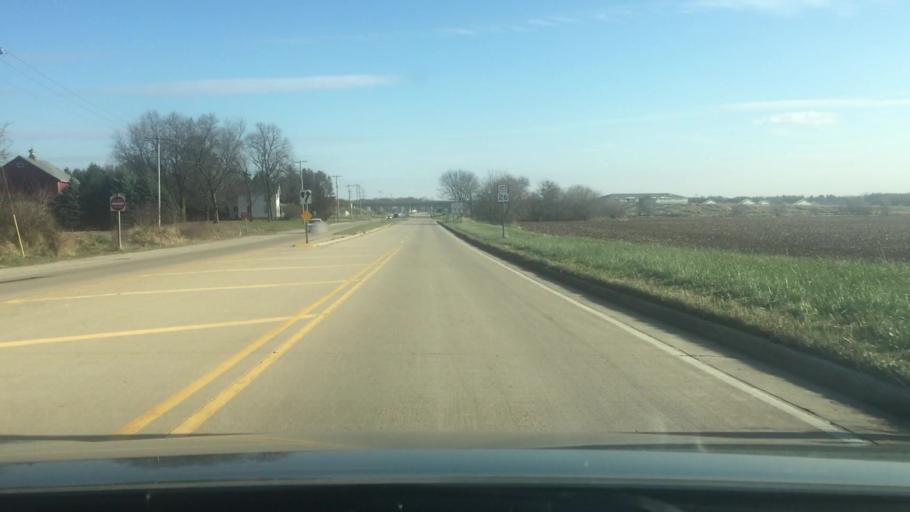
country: US
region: Wisconsin
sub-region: Jefferson County
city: Fort Atkinson
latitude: 42.9459
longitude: -88.8705
